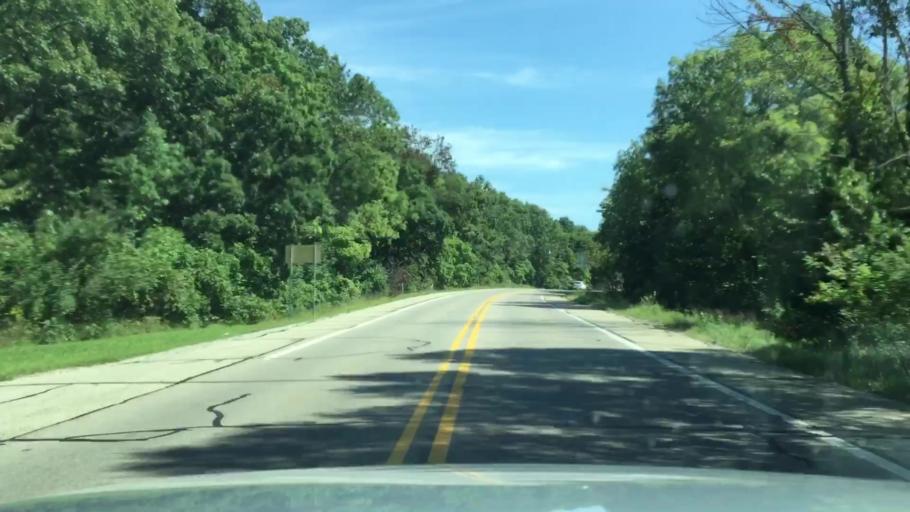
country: US
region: Michigan
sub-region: Washtenaw County
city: Manchester
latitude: 42.0605
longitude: -84.1241
